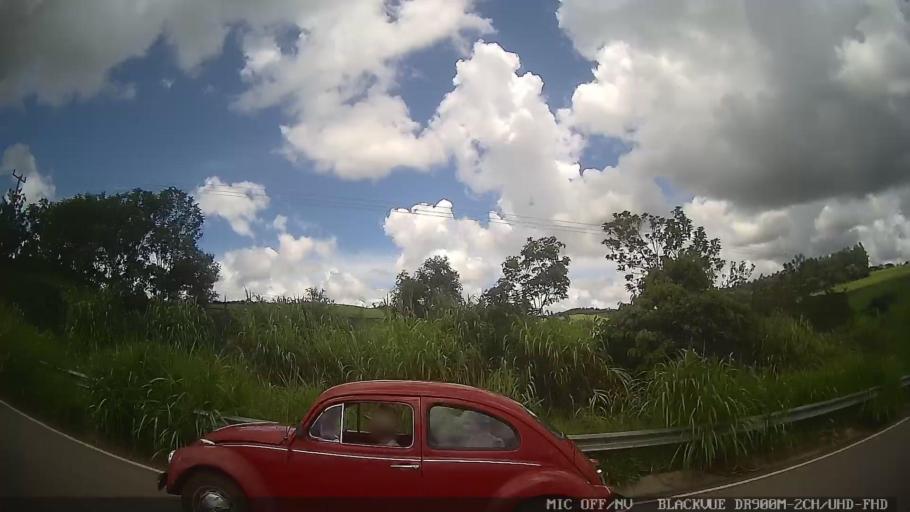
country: BR
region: Sao Paulo
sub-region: Braganca Paulista
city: Braganca Paulista
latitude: -22.8375
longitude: -46.6507
